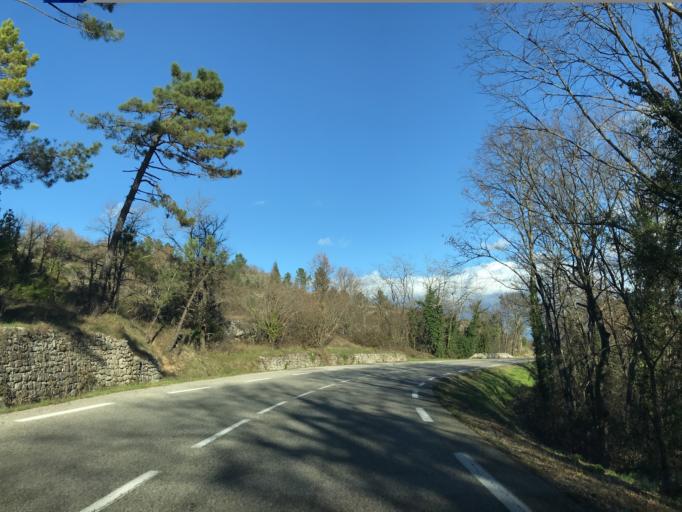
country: FR
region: Rhone-Alpes
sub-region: Departement de l'Ardeche
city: Lablachere
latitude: 44.4417
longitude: 4.2020
